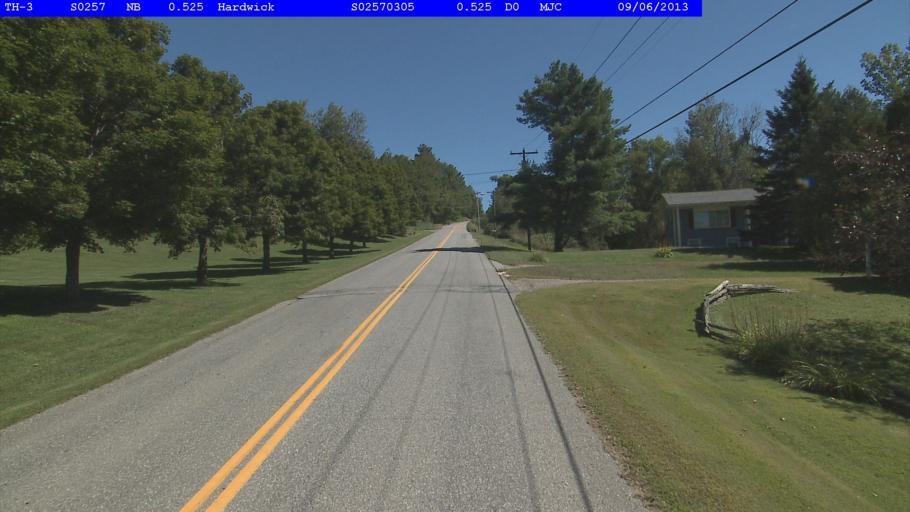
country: US
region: Vermont
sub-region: Caledonia County
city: Hardwick
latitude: 44.5056
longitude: -72.3578
